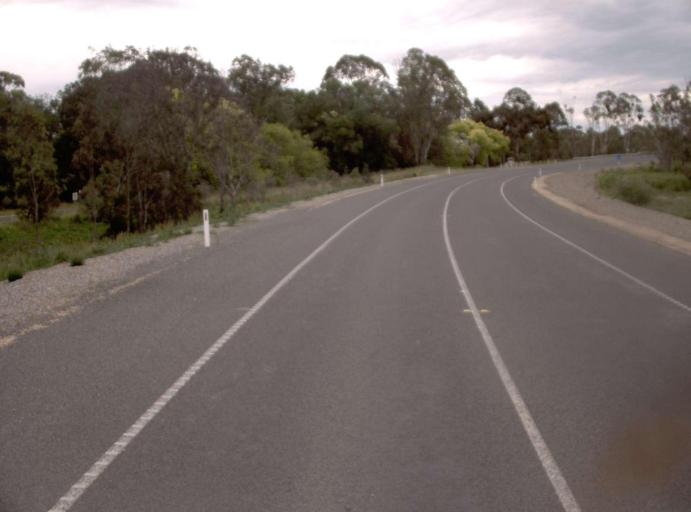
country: AU
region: Victoria
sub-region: Wellington
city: Sale
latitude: -38.1305
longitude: 147.0717
